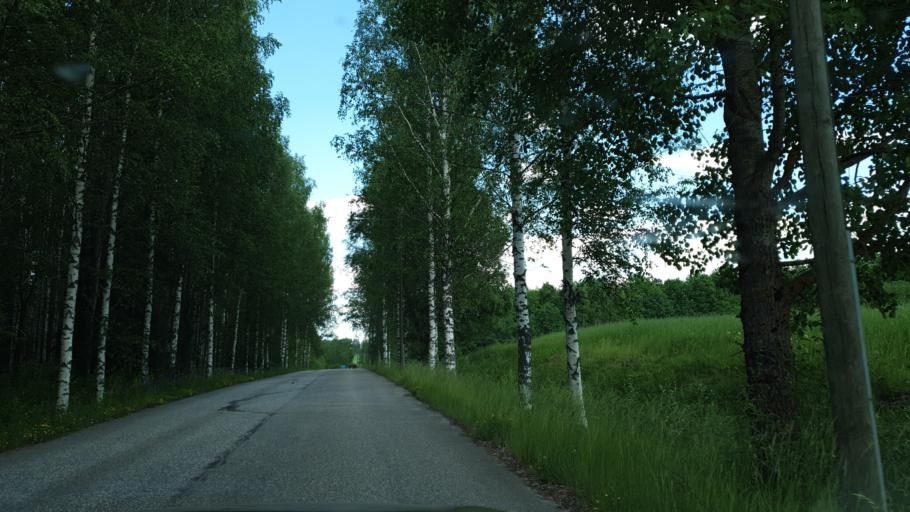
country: FI
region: Uusimaa
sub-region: Helsinki
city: Vihti
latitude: 60.3798
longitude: 24.5124
